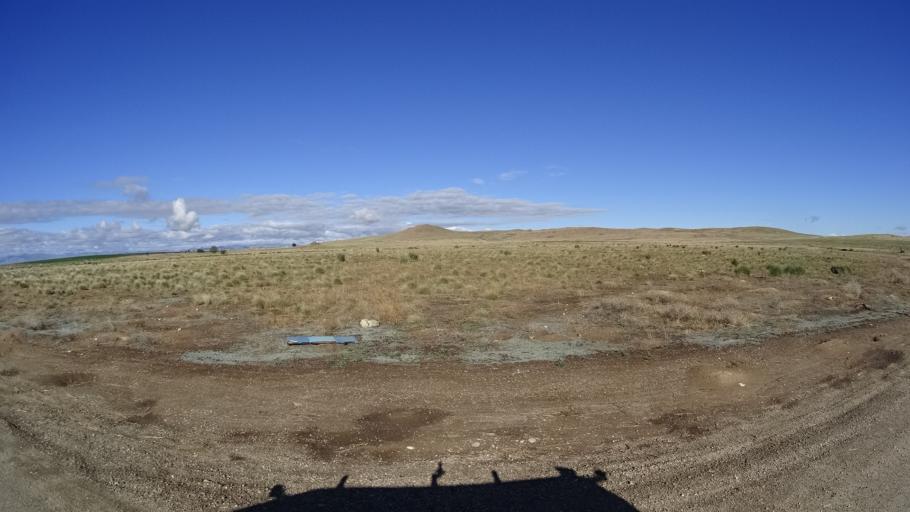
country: US
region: Idaho
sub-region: Ada County
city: Kuna
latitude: 43.4346
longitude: -116.4140
